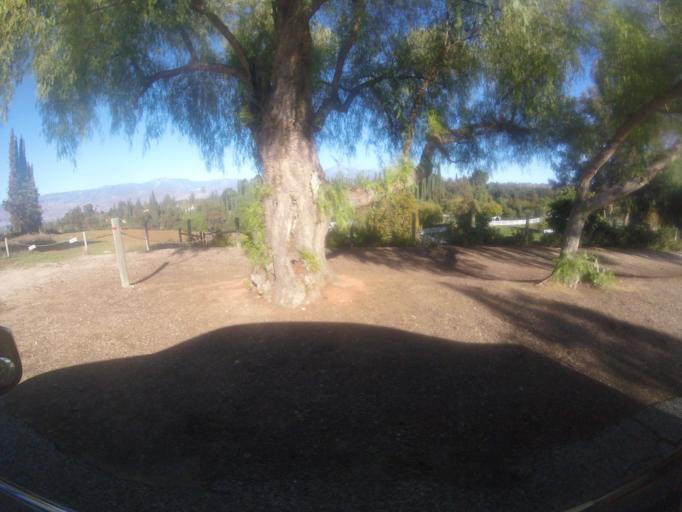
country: US
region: California
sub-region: San Bernardino County
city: Redlands
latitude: 34.0261
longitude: -117.1837
